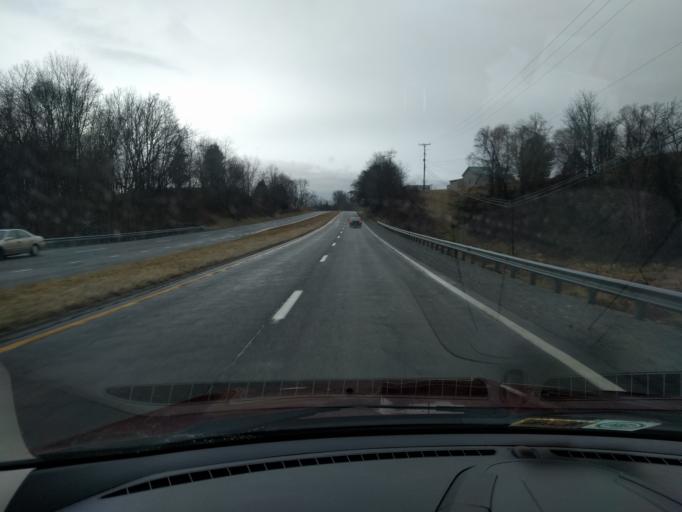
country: US
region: Virginia
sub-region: Giles County
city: Pembroke
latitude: 37.3007
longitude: -80.5625
